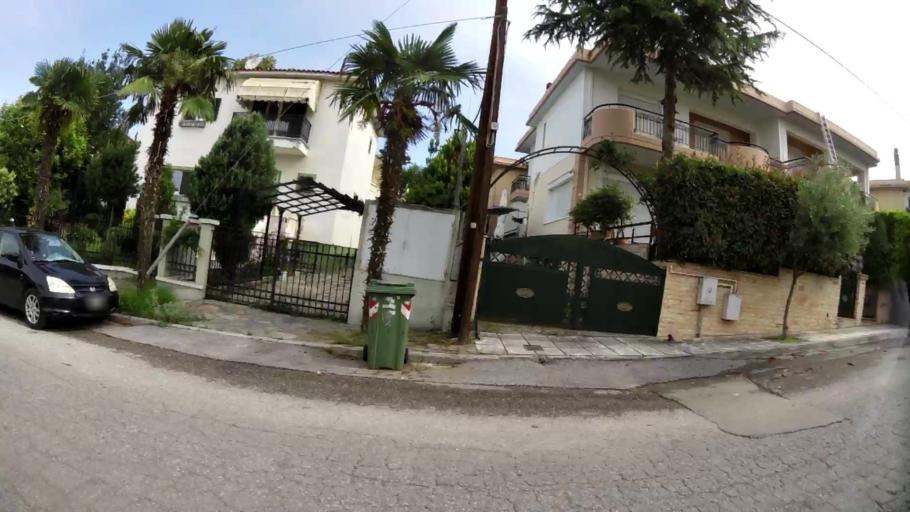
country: GR
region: Central Macedonia
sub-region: Nomos Thessalonikis
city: Panorama
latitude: 40.5848
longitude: 23.0194
